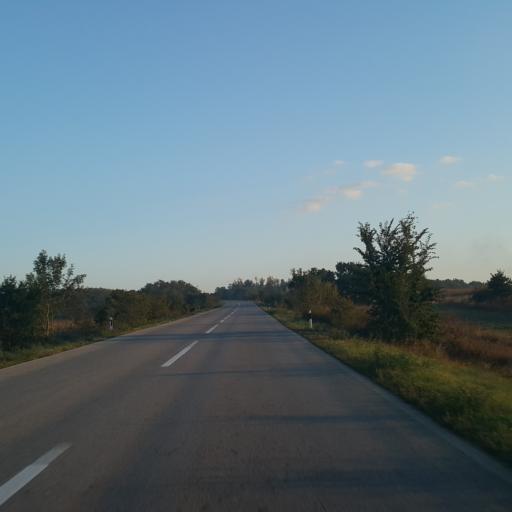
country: RS
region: Central Serbia
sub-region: Zajecarski Okrug
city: Zajecar
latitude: 44.0487
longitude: 22.3346
